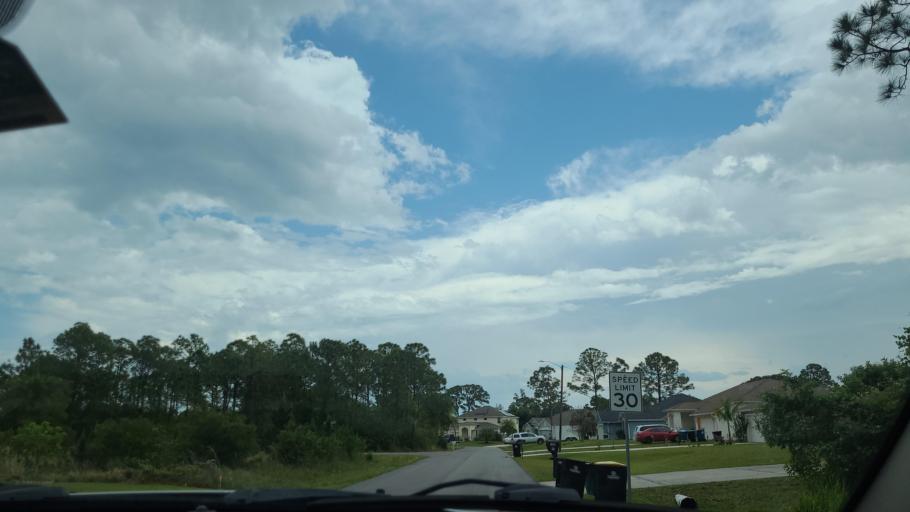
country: US
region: Florida
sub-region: Brevard County
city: Grant-Valkaria
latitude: 27.9386
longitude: -80.6317
